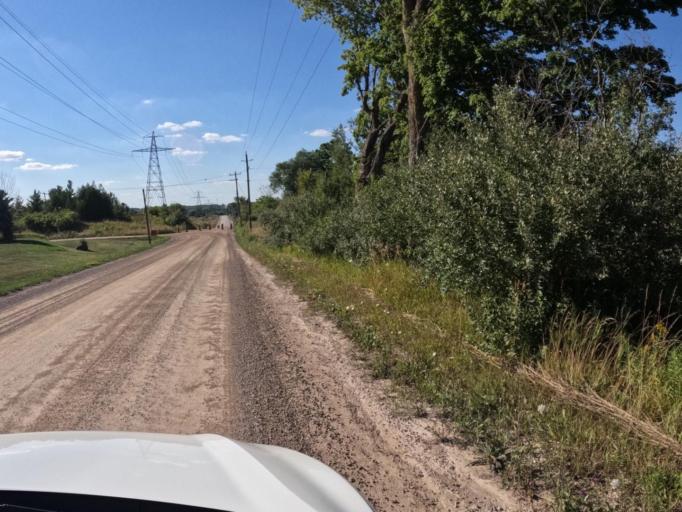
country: CA
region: Ontario
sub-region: Wellington County
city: Guelph
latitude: 43.4431
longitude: -80.1471
